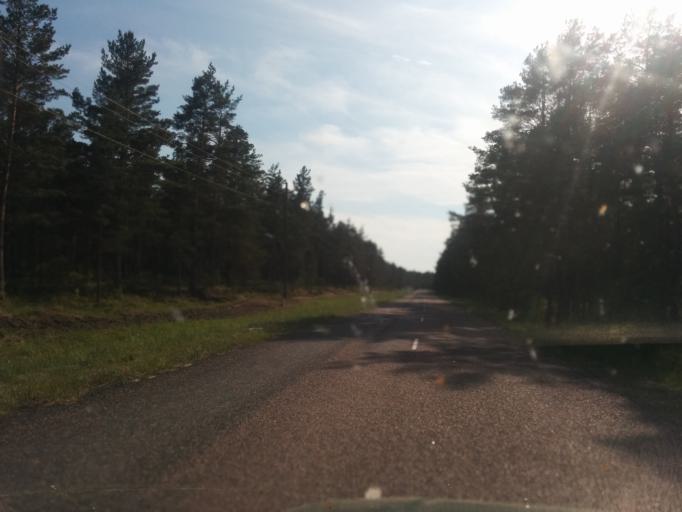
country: LV
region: Dundaga
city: Dundaga
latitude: 57.6593
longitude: 22.2857
